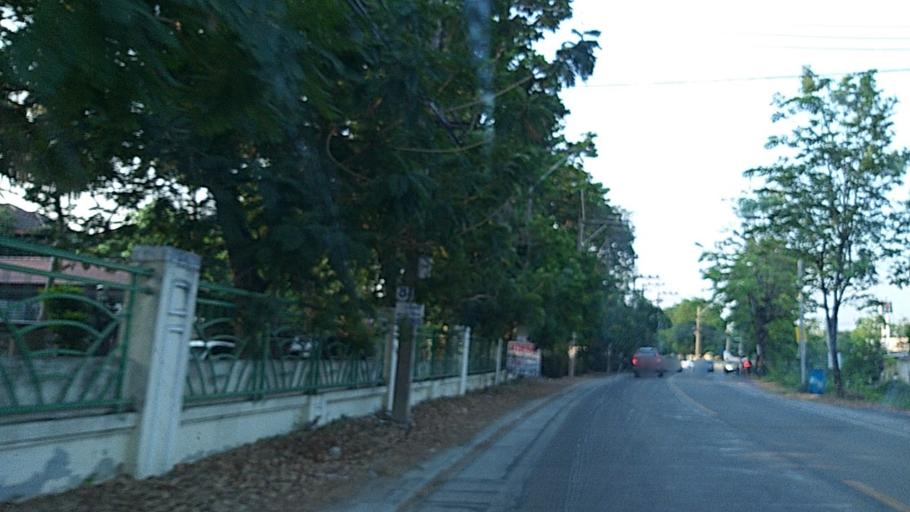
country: TH
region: Phra Nakhon Si Ayutthaya
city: Ban Bang Kadi Pathum Thani
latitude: 14.0001
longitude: 100.5639
